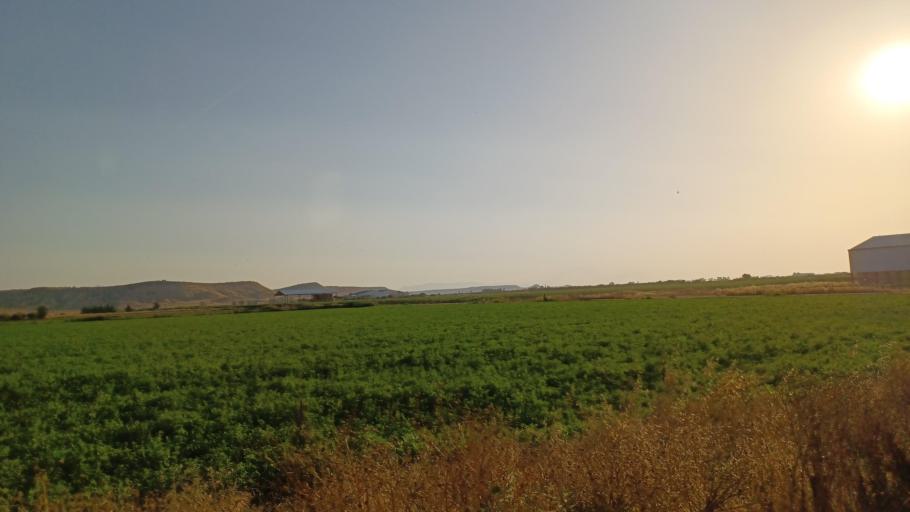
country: CY
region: Larnaka
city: Athienou
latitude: 35.0550
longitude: 33.5026
